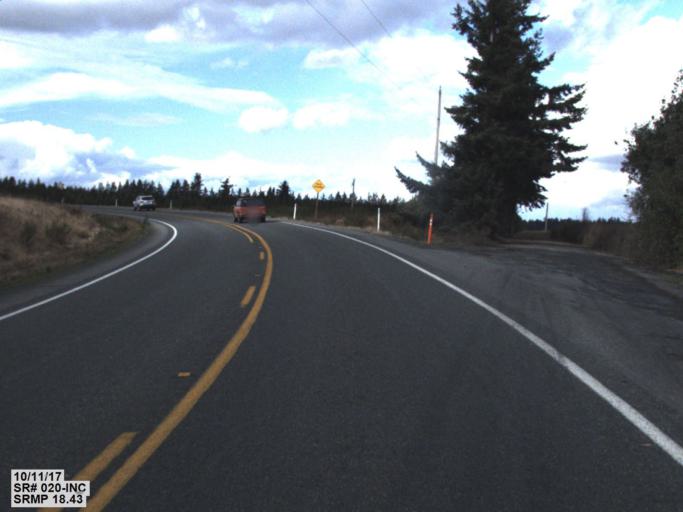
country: US
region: Washington
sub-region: Island County
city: Coupeville
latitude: 48.1960
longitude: -122.6267
